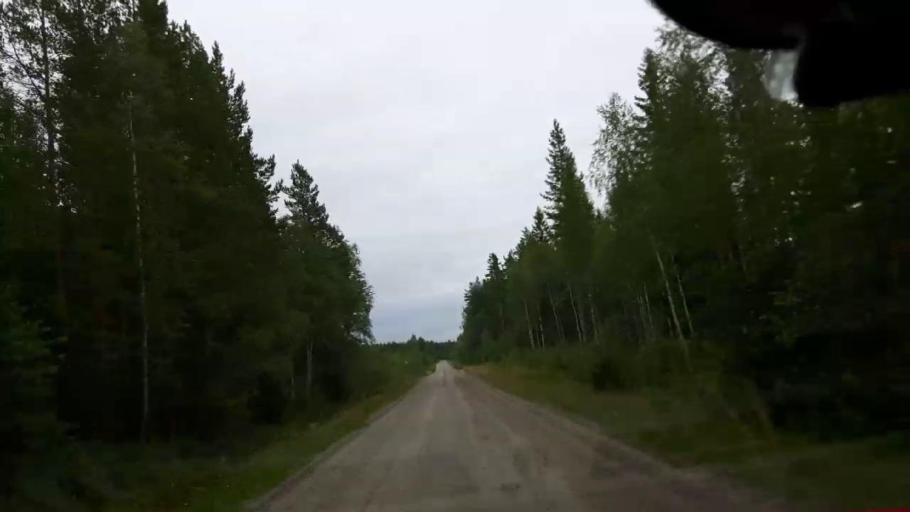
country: SE
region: Vaesternorrland
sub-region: Ange Kommun
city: Ange
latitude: 62.8084
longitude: 15.7398
